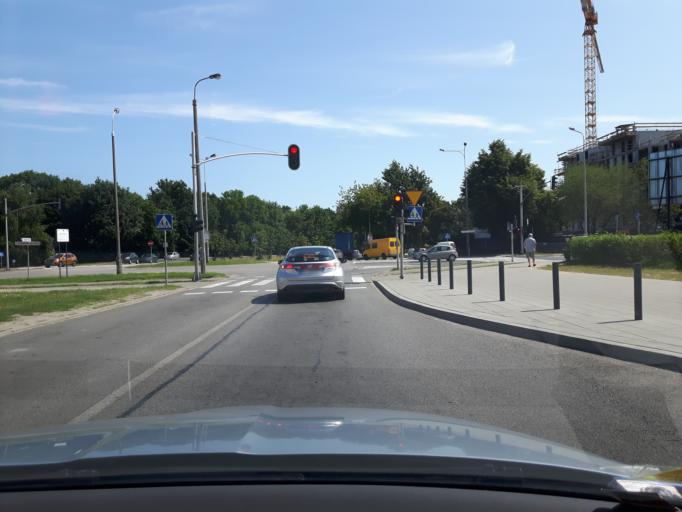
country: PL
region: Pomeranian Voivodeship
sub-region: Sopot
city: Sopot
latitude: 54.4103
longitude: 18.6035
